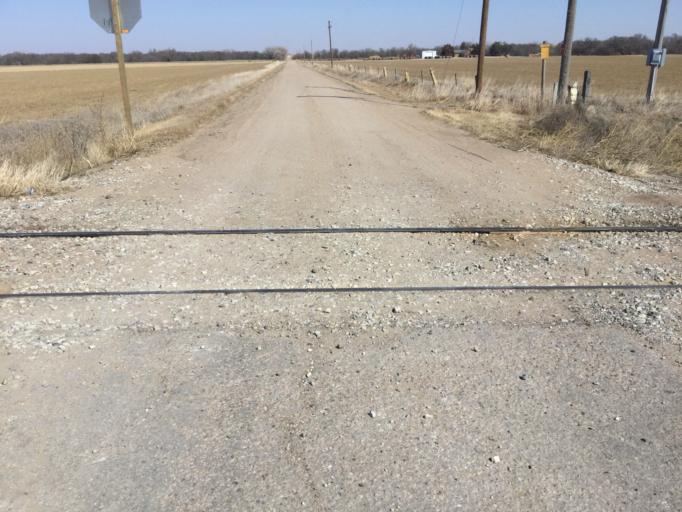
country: US
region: Kansas
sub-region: Rush County
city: La Crosse
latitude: 38.4711
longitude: -99.4010
